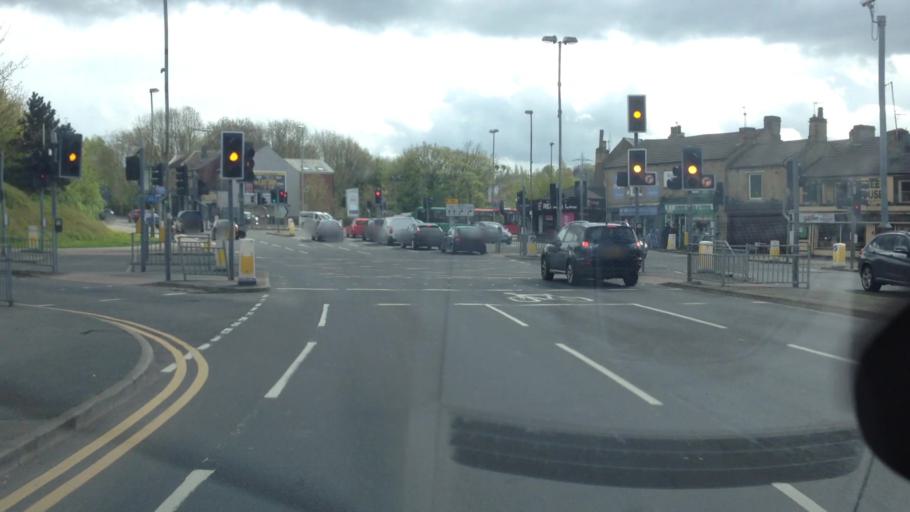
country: GB
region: England
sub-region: City and Borough of Leeds
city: Horsforth
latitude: 53.8162
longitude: -1.6022
